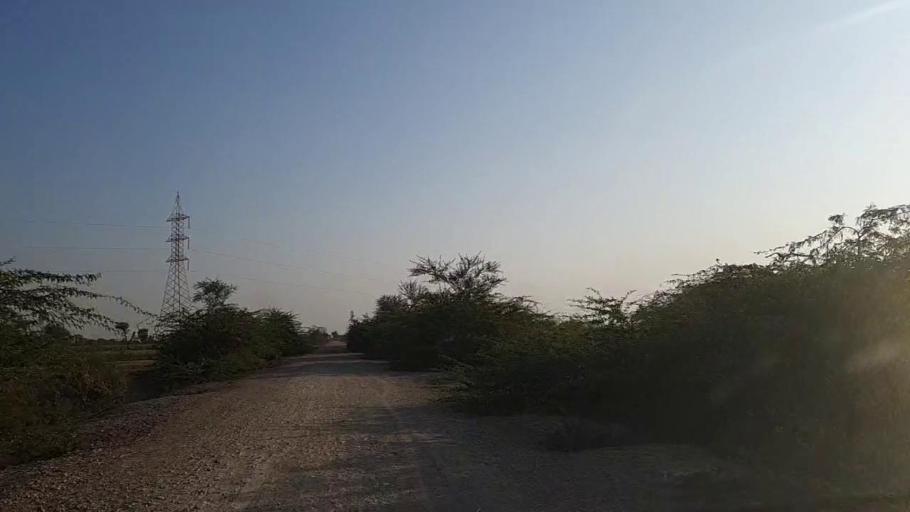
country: PK
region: Sindh
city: Naukot
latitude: 24.9259
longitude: 69.4459
